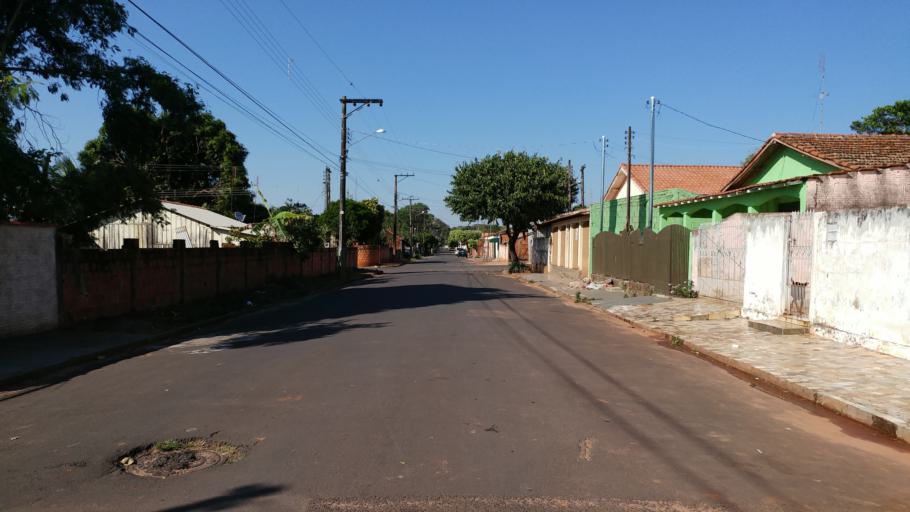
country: BR
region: Sao Paulo
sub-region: Paraguacu Paulista
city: Paraguacu Paulista
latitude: -22.4162
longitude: -50.5699
